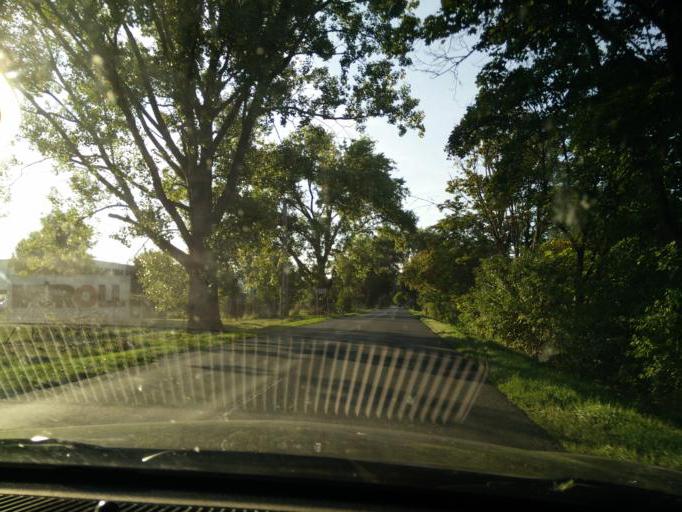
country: HU
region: Pest
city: Zsambek
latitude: 47.5359
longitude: 18.7259
